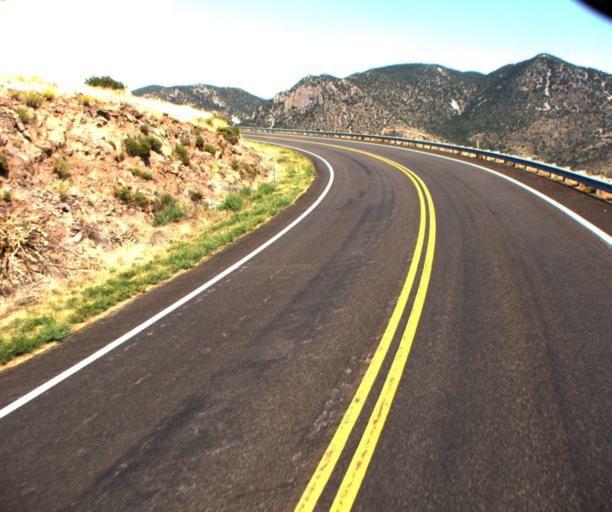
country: US
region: Arizona
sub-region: Greenlee County
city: Clifton
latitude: 33.0470
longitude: -109.1061
